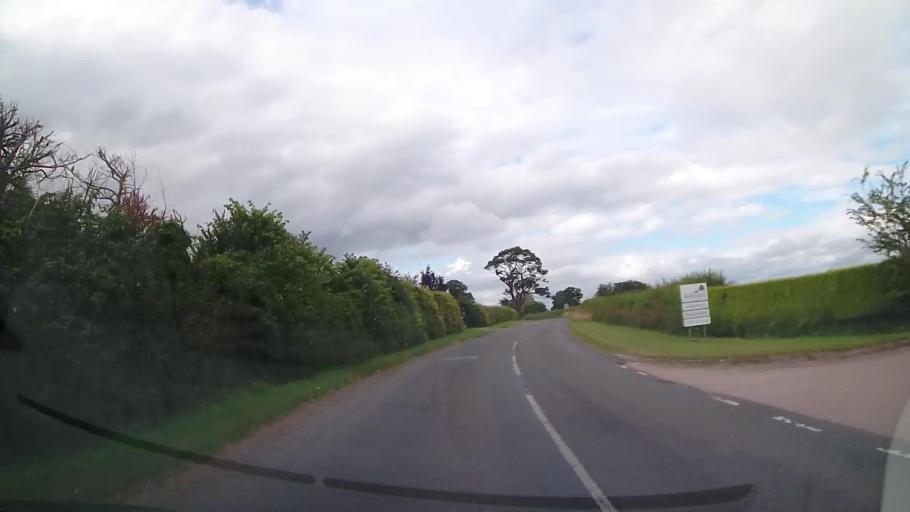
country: GB
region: England
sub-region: Shropshire
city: Wem
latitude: 52.8822
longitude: -2.7155
